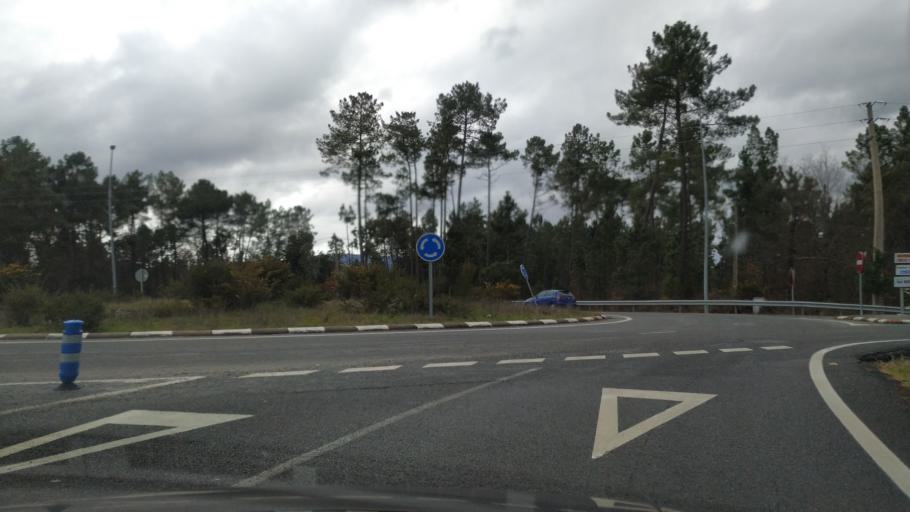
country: ES
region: Galicia
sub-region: Provincia de Ourense
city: Maside
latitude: 42.4527
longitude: -8.0276
